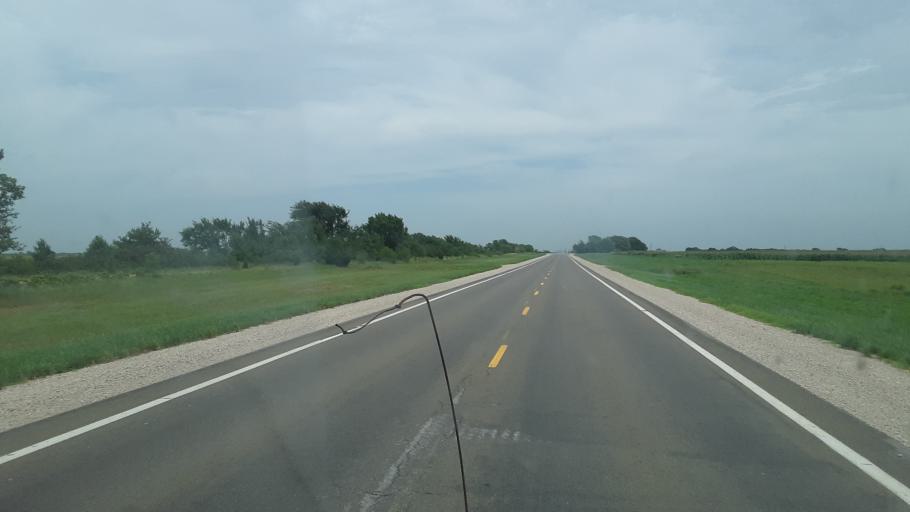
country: US
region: Kansas
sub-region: Woodson County
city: Yates Center
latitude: 37.9120
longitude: -95.5807
